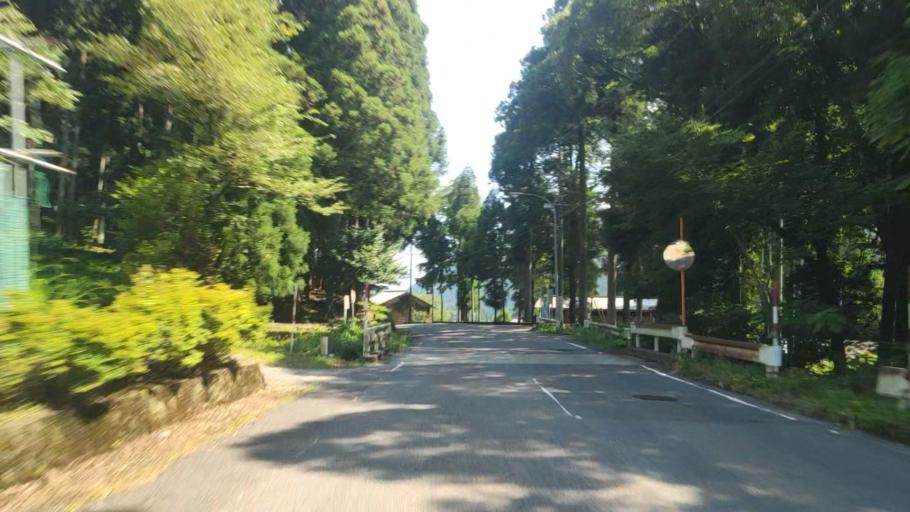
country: JP
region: Gifu
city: Godo
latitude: 35.6289
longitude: 136.6185
